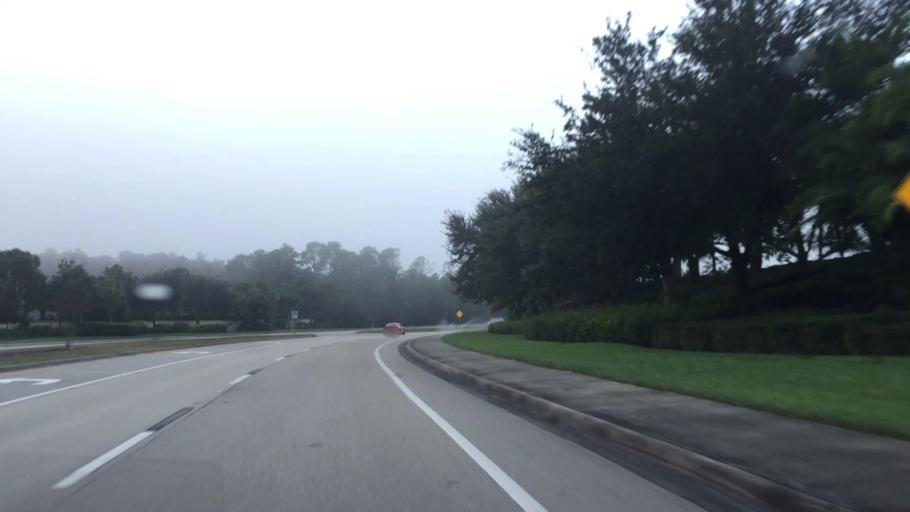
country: US
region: Florida
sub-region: Lee County
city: Gateway
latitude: 26.5762
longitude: -81.7790
